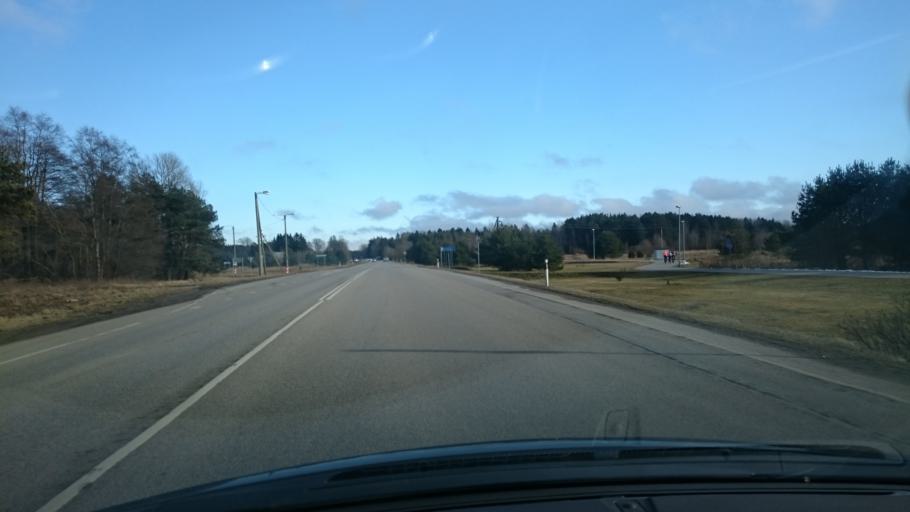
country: EE
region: Harju
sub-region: Harku vald
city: Tabasalu
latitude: 59.4341
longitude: 24.5885
